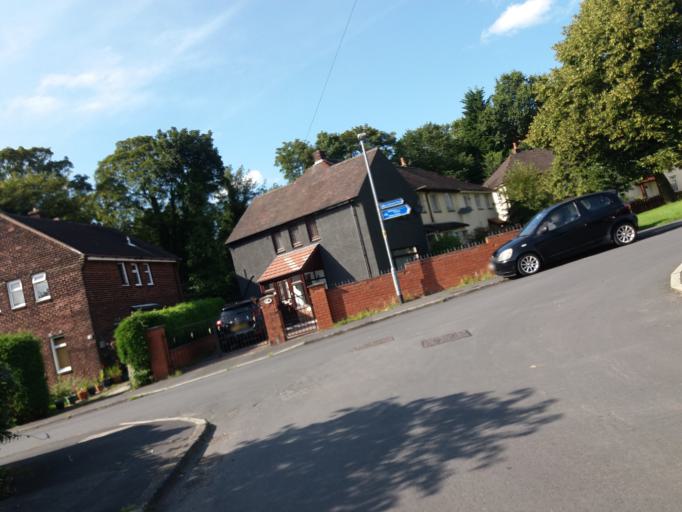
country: GB
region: England
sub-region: Lancashire
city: Coppull
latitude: 53.6442
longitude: -2.6450
